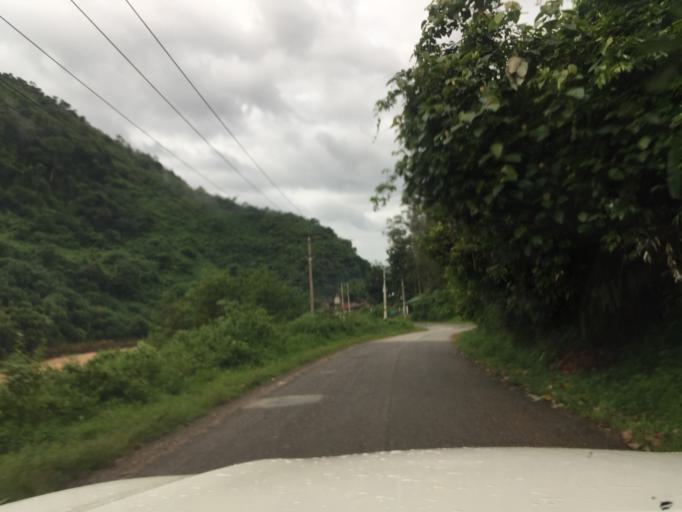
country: LA
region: Oudomxai
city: Muang La
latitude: 20.9888
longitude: 102.2276
